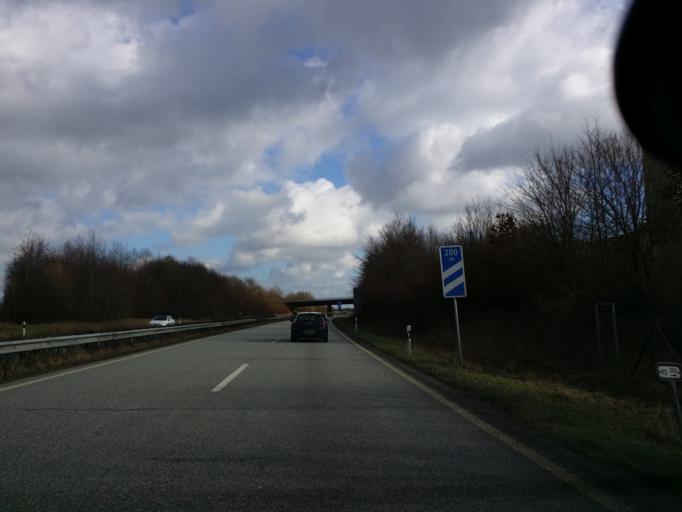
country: DE
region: Schleswig-Holstein
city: Bredenbek
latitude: 54.3178
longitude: 9.8496
